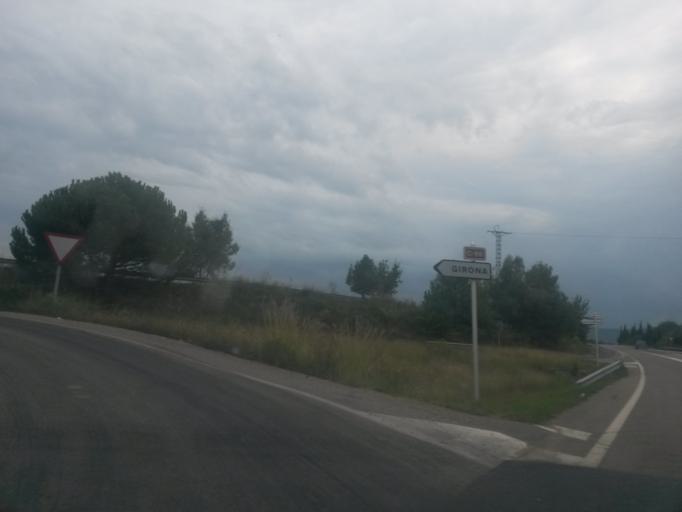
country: ES
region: Catalonia
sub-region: Provincia de Girona
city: Banyoles
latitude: 42.1396
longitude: 2.7639
